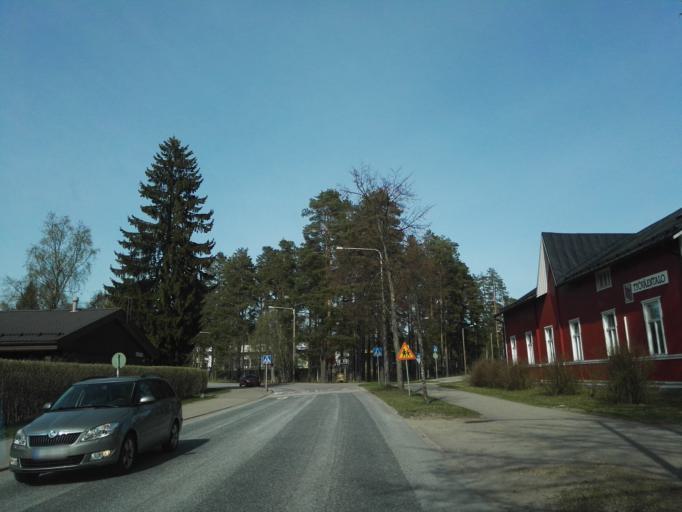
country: FI
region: Central Finland
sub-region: Joutsa
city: Joutsa
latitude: 61.7447
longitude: 26.1197
